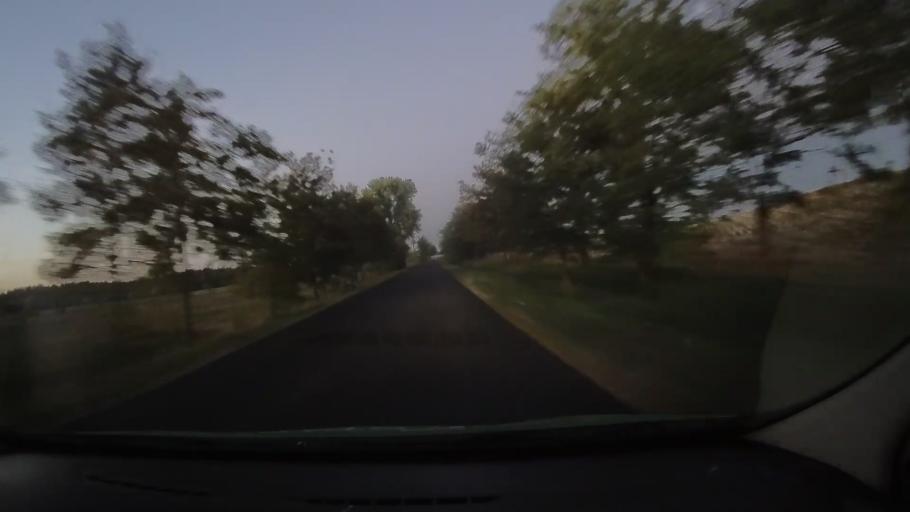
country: RO
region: Bihor
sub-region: Comuna Simian
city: Simian
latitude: 47.5060
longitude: 22.0941
